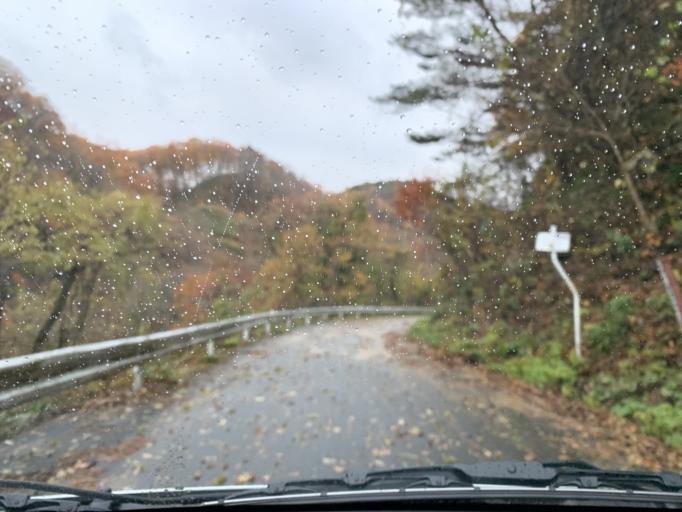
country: JP
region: Iwate
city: Mizusawa
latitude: 39.1018
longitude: 140.9400
